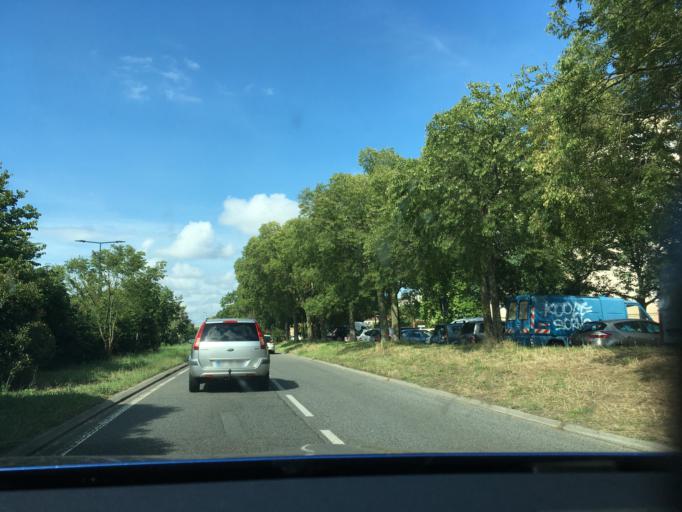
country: FR
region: Midi-Pyrenees
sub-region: Departement de la Haute-Garonne
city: Blagnac
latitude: 43.5805
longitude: 1.3959
